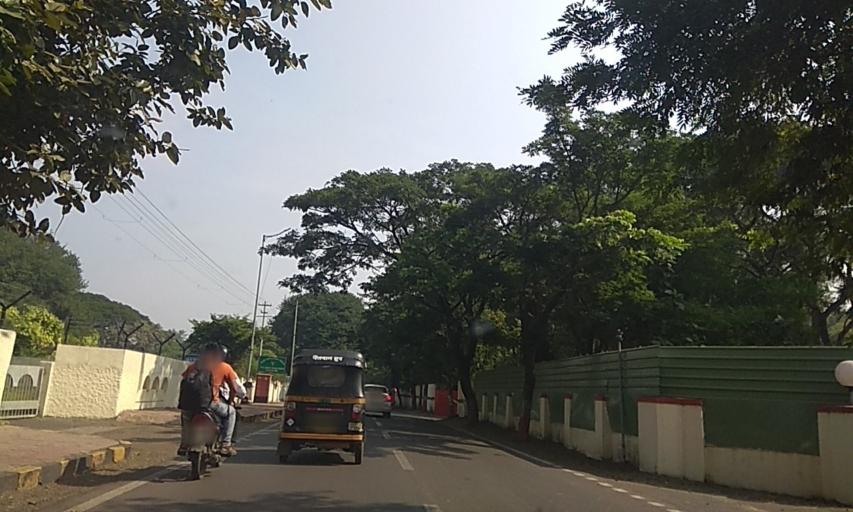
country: IN
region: Maharashtra
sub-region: Pune Division
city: Khadki
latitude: 18.5580
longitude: 73.8501
